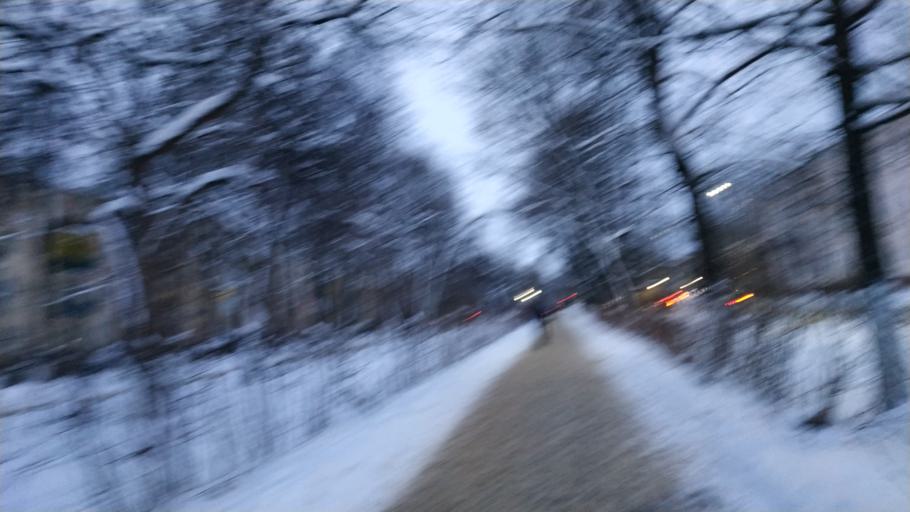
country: RU
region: Moskovskaya
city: Shchelkovo
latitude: 55.9243
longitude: 37.9793
